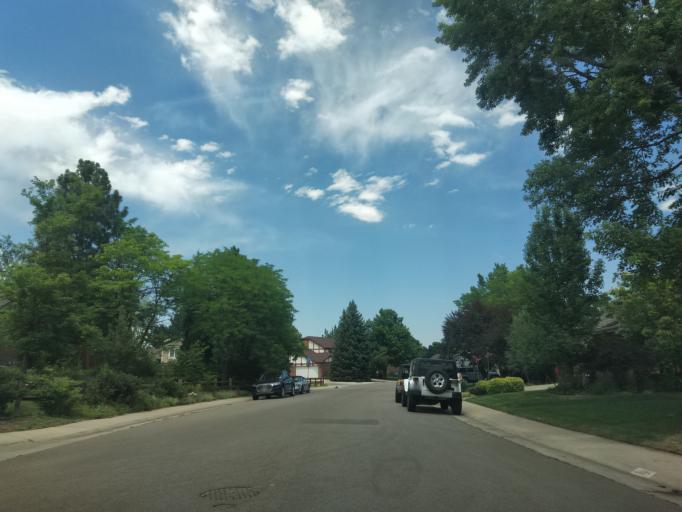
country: US
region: Colorado
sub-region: Jefferson County
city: Lakewood
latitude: 39.6777
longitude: -105.1030
